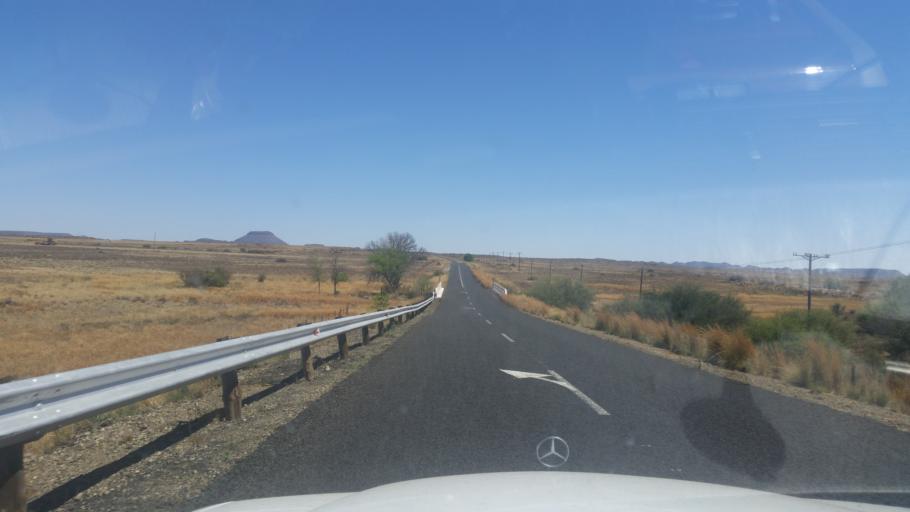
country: ZA
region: Northern Cape
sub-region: Pixley ka Seme District Municipality
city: Colesberg
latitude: -30.7024
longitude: 25.1927
